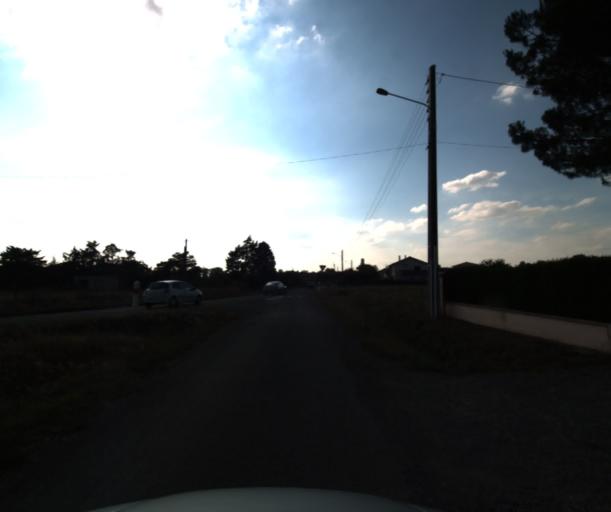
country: FR
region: Midi-Pyrenees
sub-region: Departement de la Haute-Garonne
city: Saint-Lys
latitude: 43.5057
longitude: 1.1927
